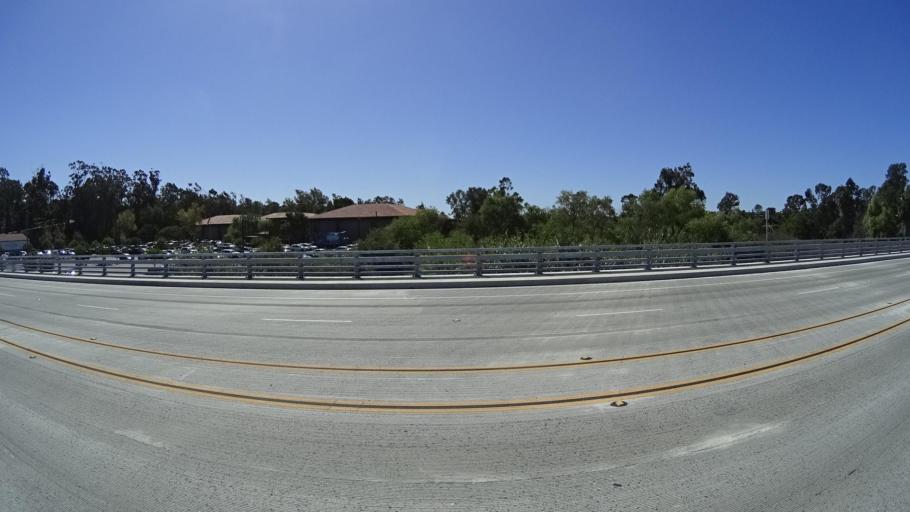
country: US
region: California
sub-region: San Diego County
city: Bonita
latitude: 32.6593
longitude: -117.0423
